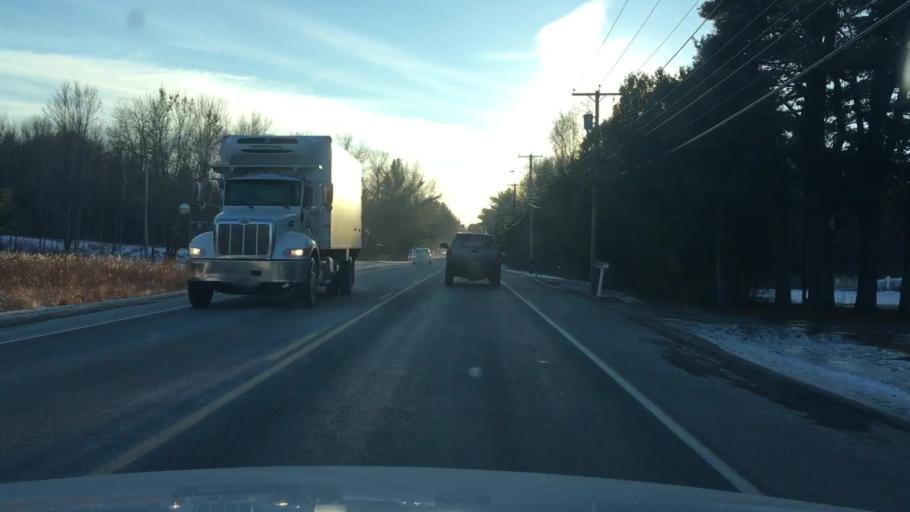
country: US
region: Maine
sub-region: Penobscot County
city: Brewer
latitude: 44.8106
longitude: -68.7359
